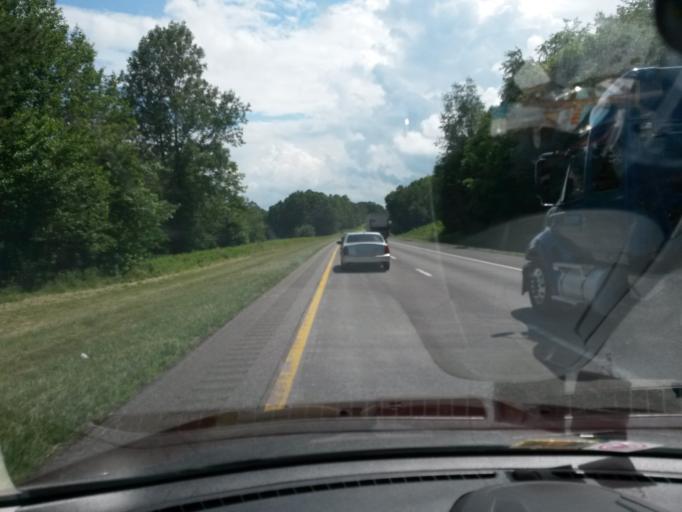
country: US
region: North Carolina
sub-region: Surry County
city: Dobson
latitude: 36.3775
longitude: -80.7912
